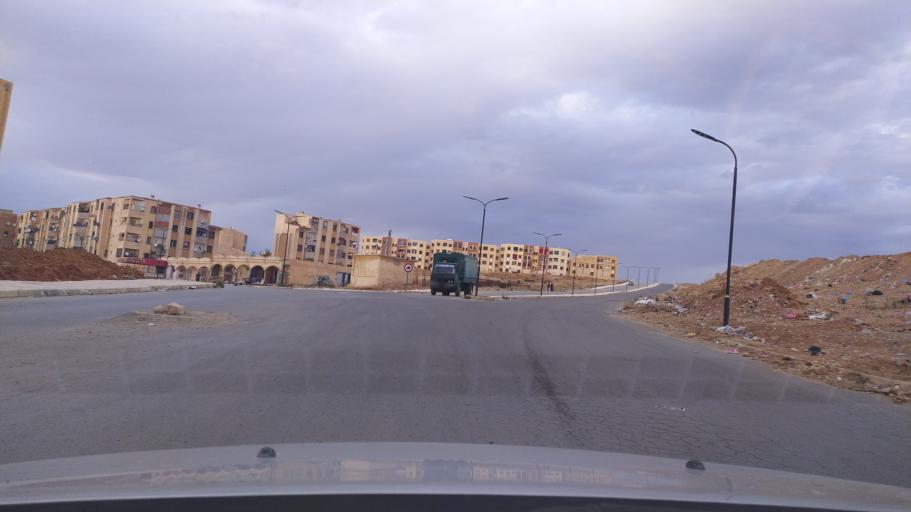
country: DZ
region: Tiaret
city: Frenda
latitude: 35.0540
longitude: 1.0625
